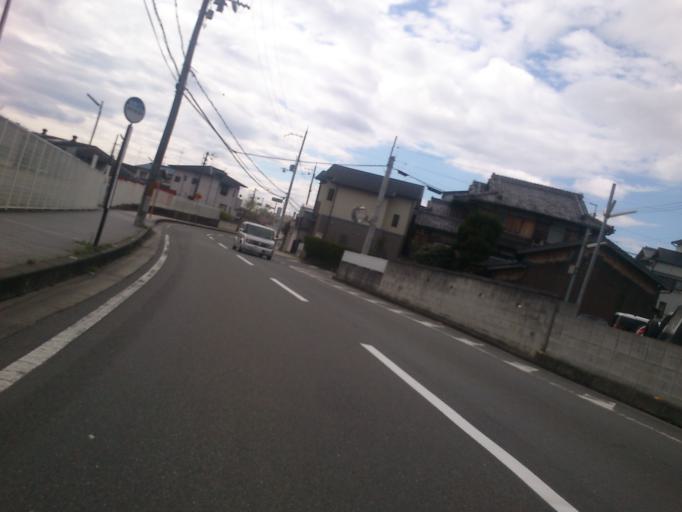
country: JP
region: Kyoto
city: Muko
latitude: 34.9181
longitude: 135.7014
